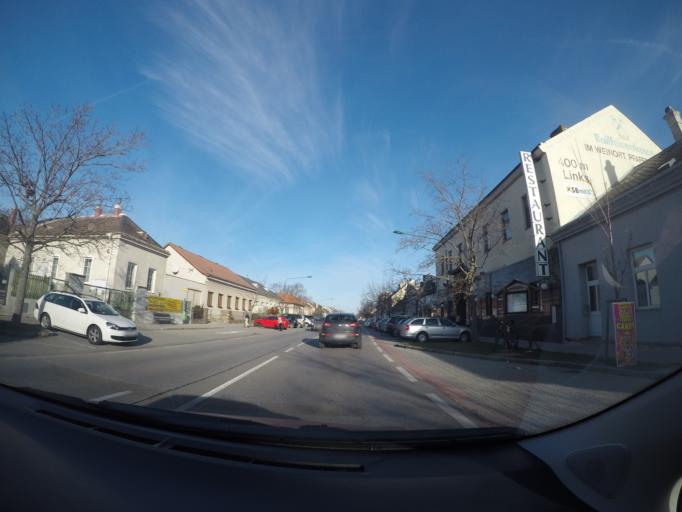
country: AT
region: Lower Austria
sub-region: Politischer Bezirk Baden
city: Pfaffstatten
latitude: 48.0144
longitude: 16.2592
